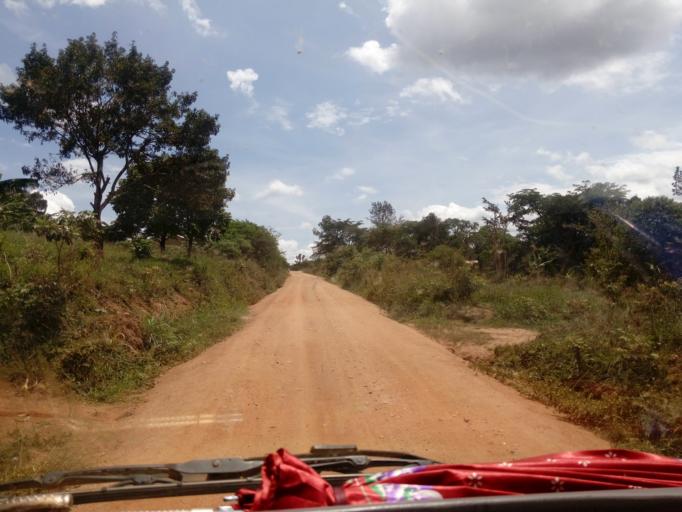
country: UG
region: Central Region
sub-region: Mubende District
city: Mubende
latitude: 0.4610
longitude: 31.7006
